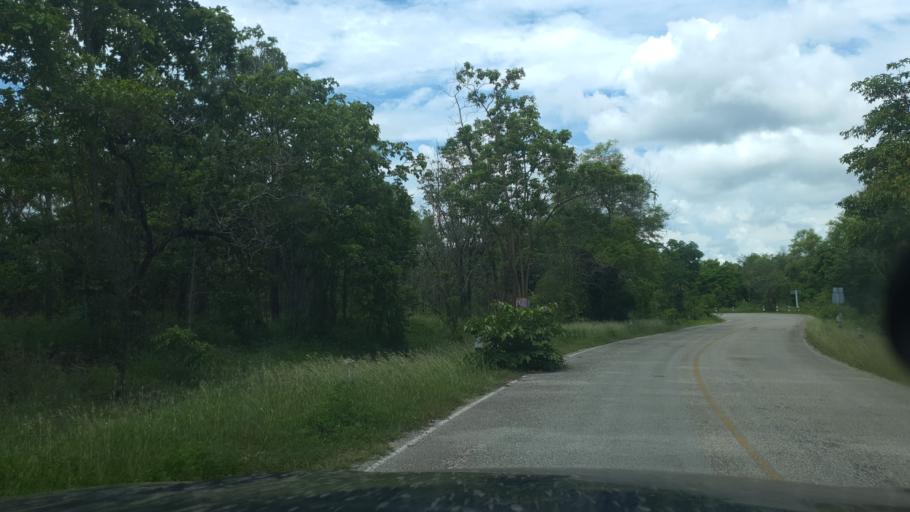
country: TH
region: Lampang
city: Soem Ngam
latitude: 18.0372
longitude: 99.3754
